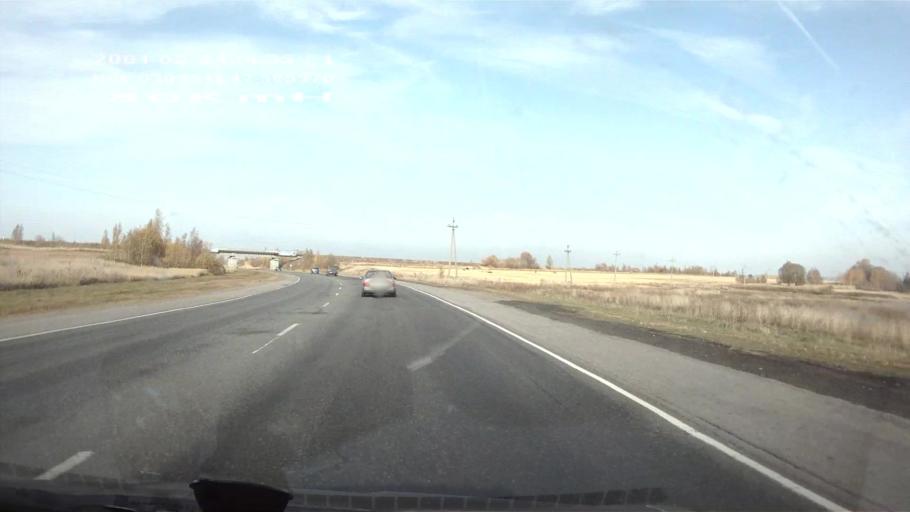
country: RU
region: Chuvashia
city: Kugesi
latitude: 56.0396
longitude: 47.3631
